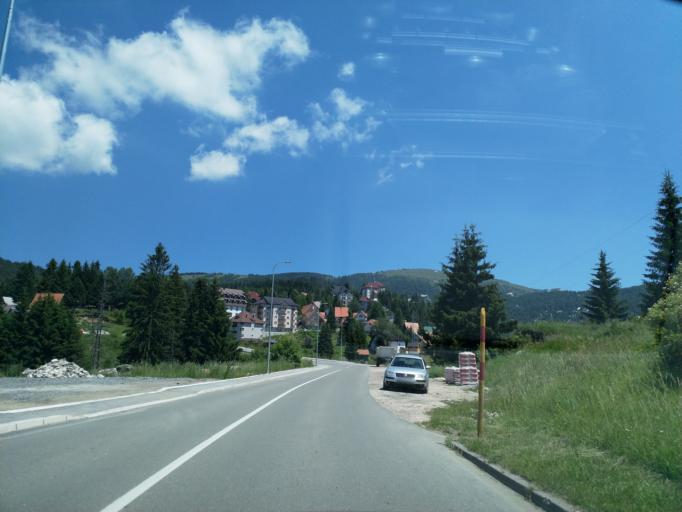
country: RS
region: Central Serbia
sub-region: Raski Okrug
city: Raska
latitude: 43.2736
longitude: 20.7763
